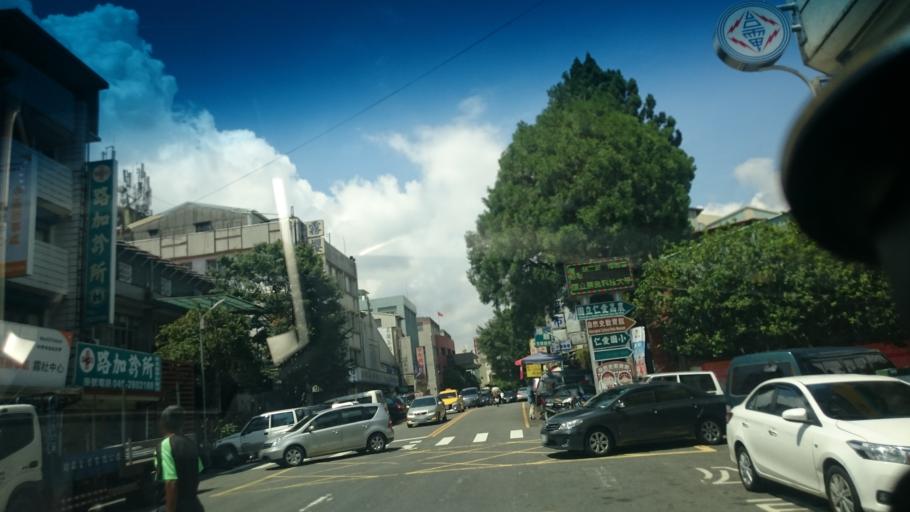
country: TW
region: Taiwan
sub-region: Nantou
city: Puli
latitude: 24.0221
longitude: 121.1321
